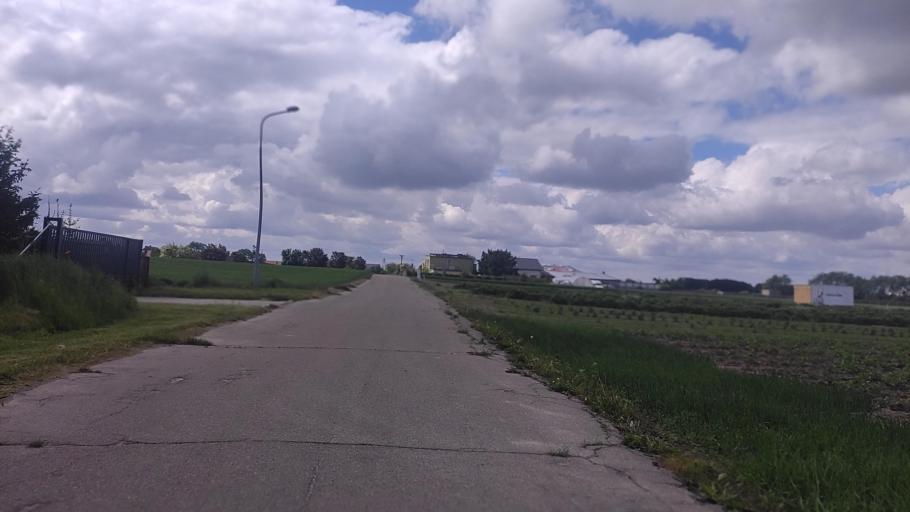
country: PL
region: Greater Poland Voivodeship
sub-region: Powiat poznanski
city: Kostrzyn
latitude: 52.4167
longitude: 17.1708
